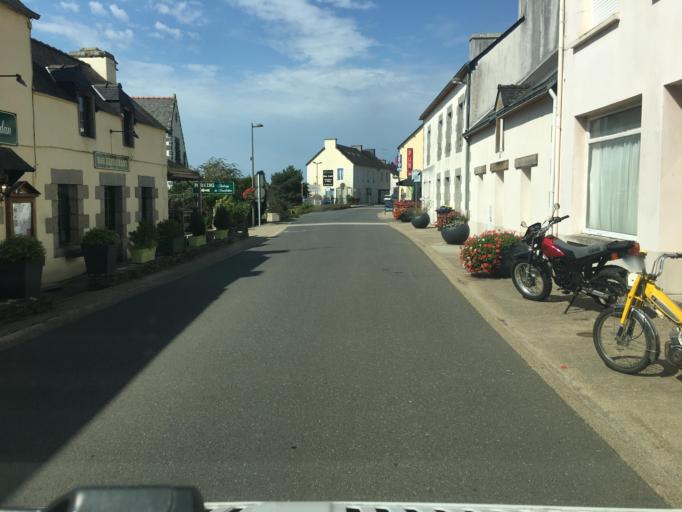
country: FR
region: Brittany
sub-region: Departement des Cotes-d'Armor
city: Mur-de-Bretagne
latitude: 48.2162
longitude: -3.0364
